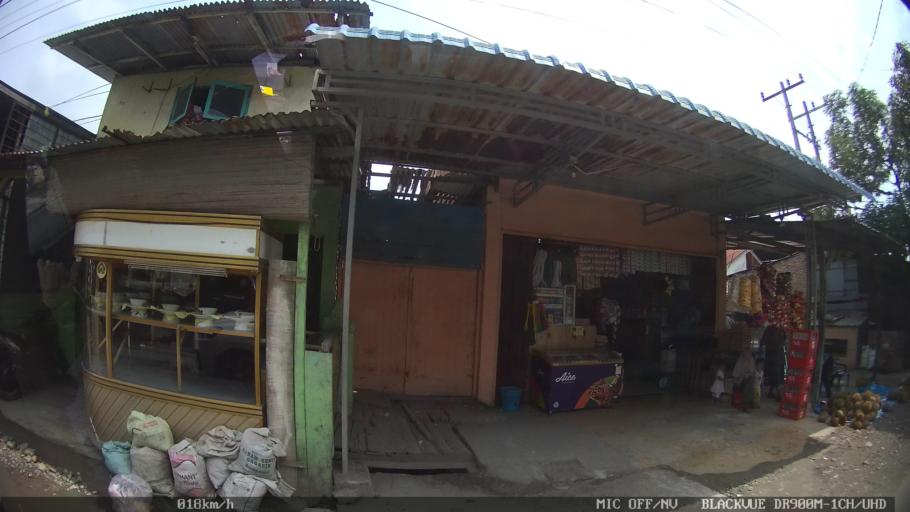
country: ID
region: North Sumatra
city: Medan
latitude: 3.6513
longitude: 98.6908
